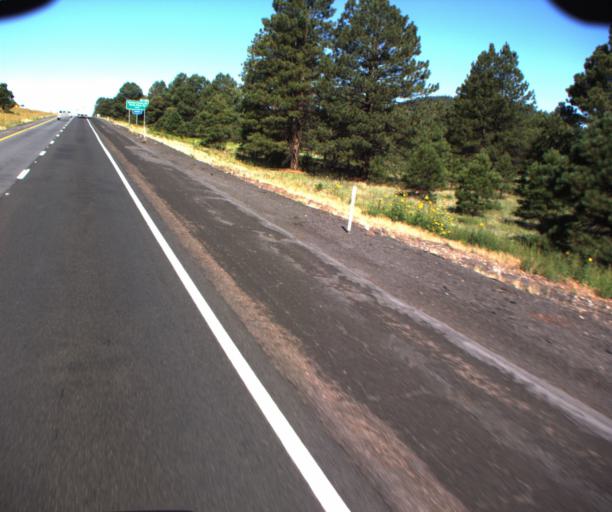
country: US
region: Arizona
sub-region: Coconino County
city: Williams
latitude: 35.2586
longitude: -112.0980
